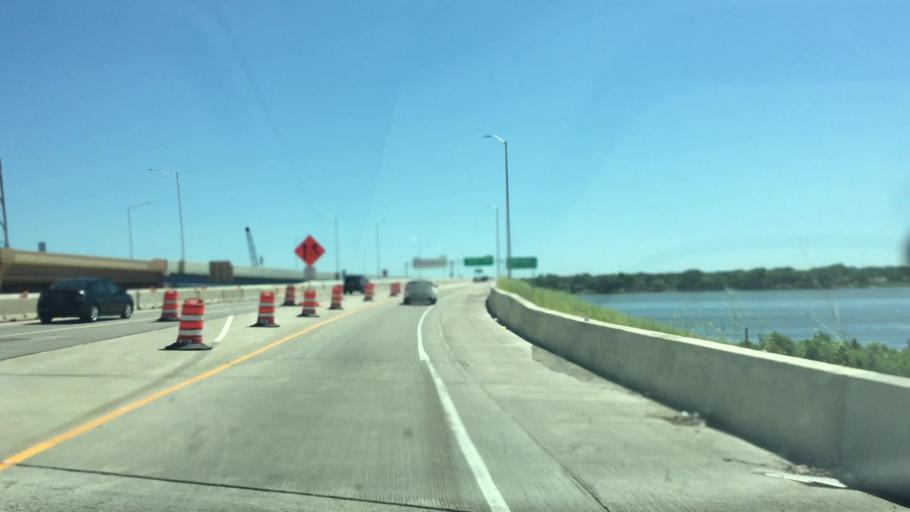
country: US
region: Wisconsin
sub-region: Winnebago County
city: Menasha
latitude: 44.2179
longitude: -88.4692
